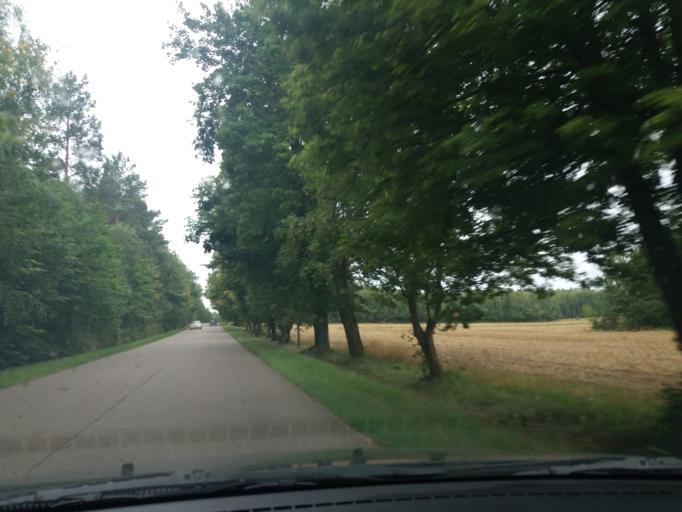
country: PL
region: Masovian Voivodeship
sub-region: Powiat mlawski
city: Wieczfnia Koscielna
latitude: 53.2104
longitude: 20.5030
